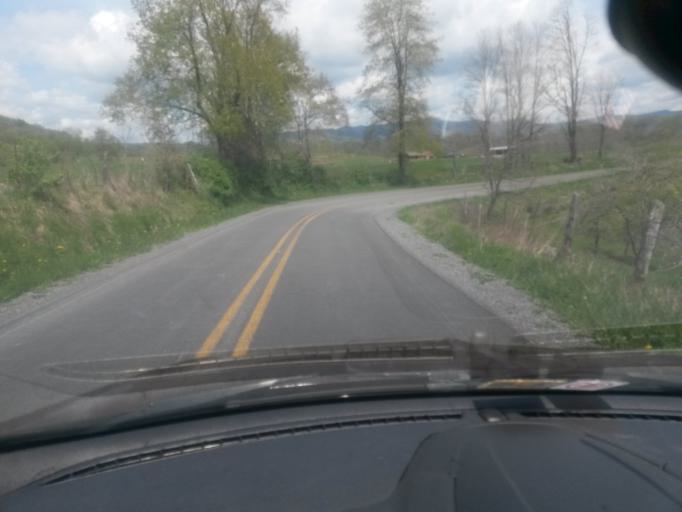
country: US
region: West Virginia
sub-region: Pocahontas County
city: Marlinton
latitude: 38.1037
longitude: -80.2259
